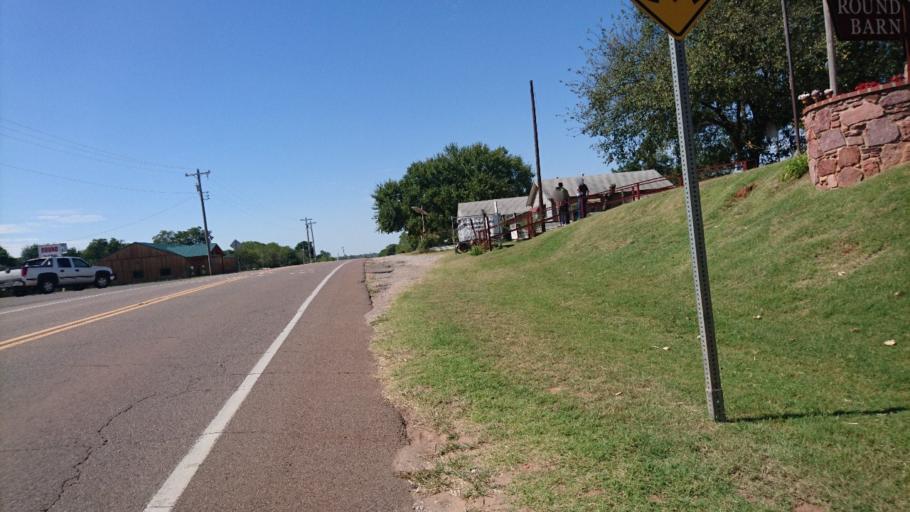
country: US
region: Oklahoma
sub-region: Oklahoma County
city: Jones
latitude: 35.6622
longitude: -97.3259
